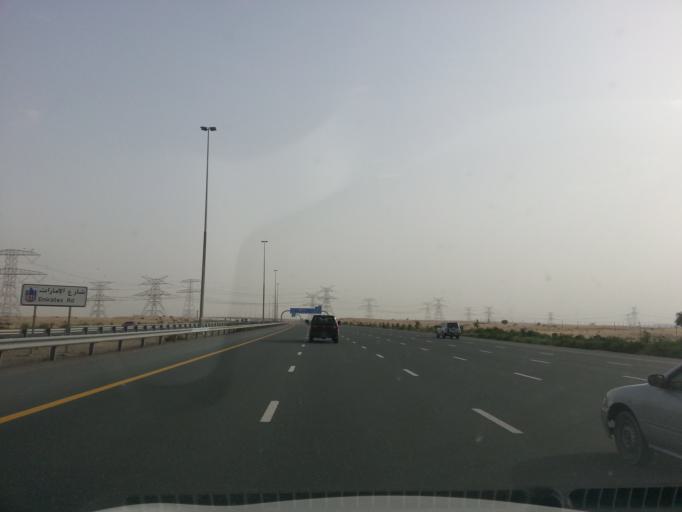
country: AE
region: Dubai
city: Dubai
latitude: 24.9892
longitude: 55.2464
